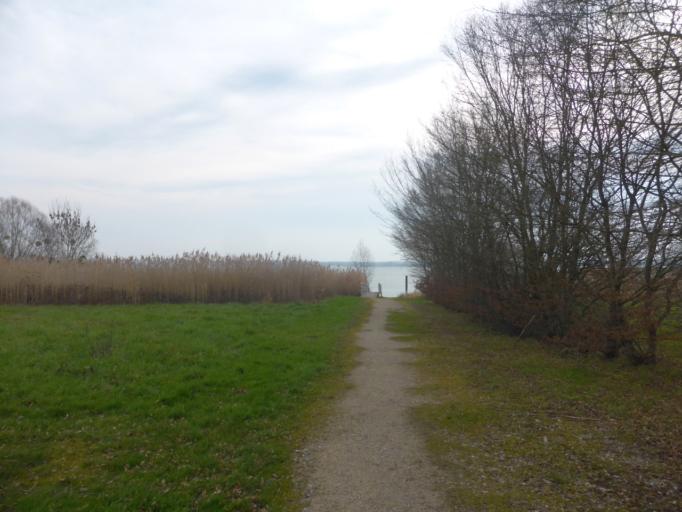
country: FR
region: Champagne-Ardenne
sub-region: Departement de l'Aube
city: Lusigny-sur-Barse
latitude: 48.2646
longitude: 4.2970
